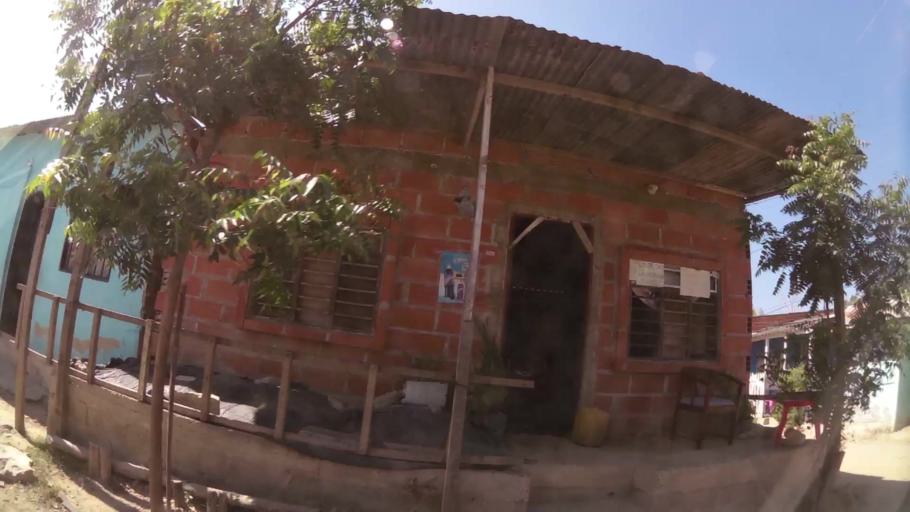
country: CO
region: Bolivar
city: Cartagena
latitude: 10.3546
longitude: -75.4855
